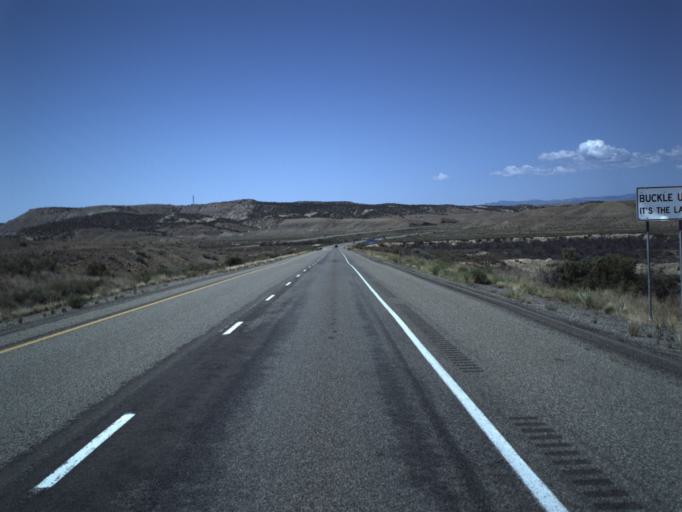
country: US
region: Colorado
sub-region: Mesa County
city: Loma
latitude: 39.1935
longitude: -109.0718
